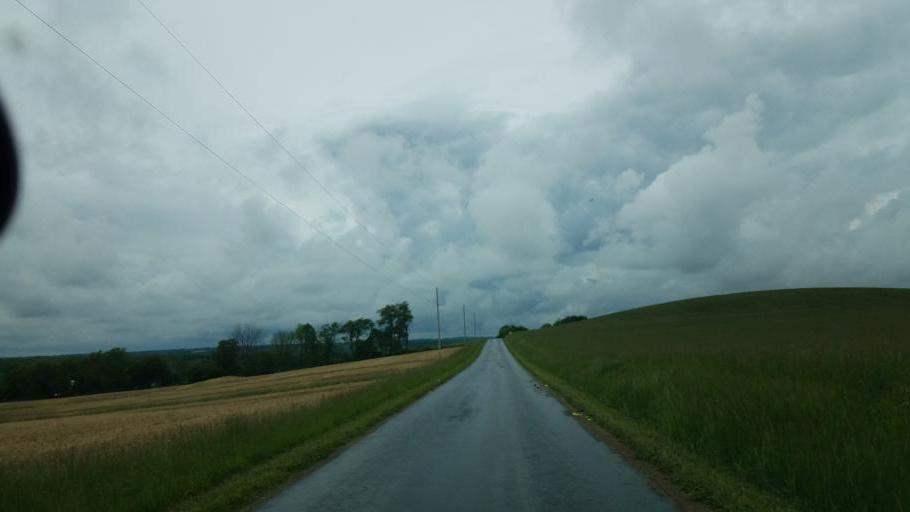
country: US
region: Ohio
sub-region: Richland County
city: Lexington
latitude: 40.6017
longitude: -82.6244
